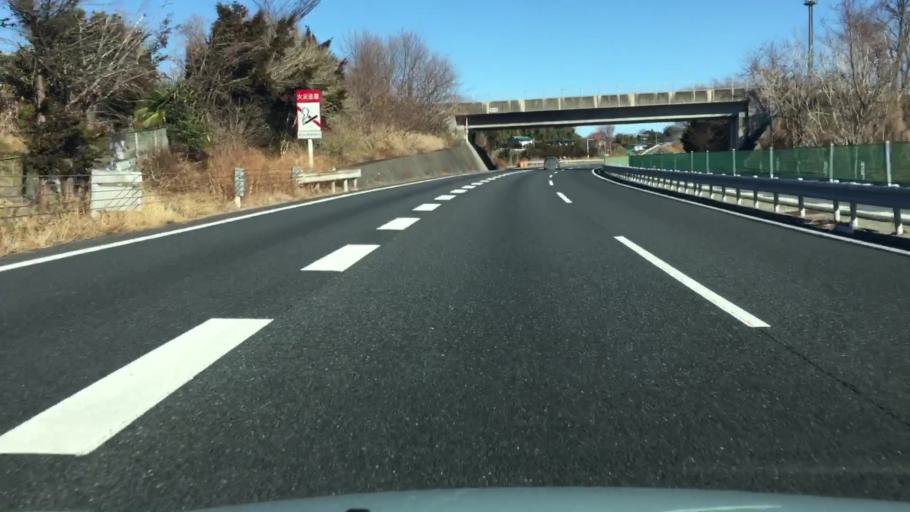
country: JP
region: Gunma
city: Shibukawa
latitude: 36.5131
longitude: 139.0324
